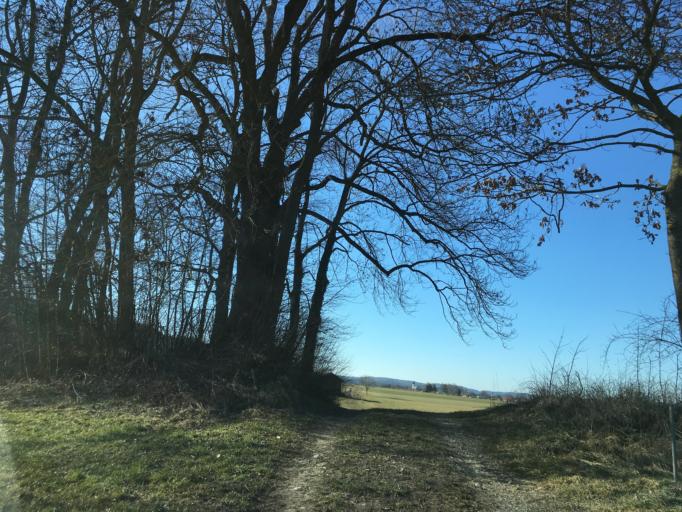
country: DE
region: Bavaria
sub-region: Upper Bavaria
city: Bruckmuhl
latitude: 47.8651
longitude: 11.9124
